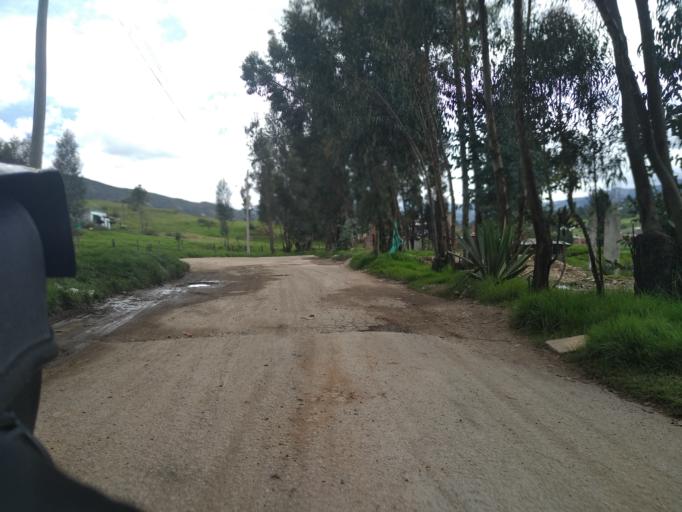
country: CO
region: Cundinamarca
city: Lenguazaque
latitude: 5.3021
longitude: -73.7125
